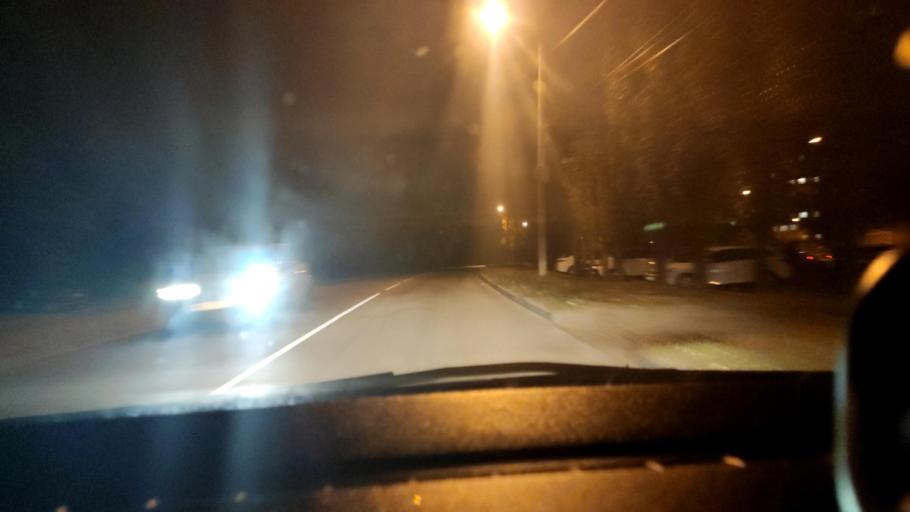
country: RU
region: Voronezj
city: Shilovo
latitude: 51.5531
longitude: 39.0904
